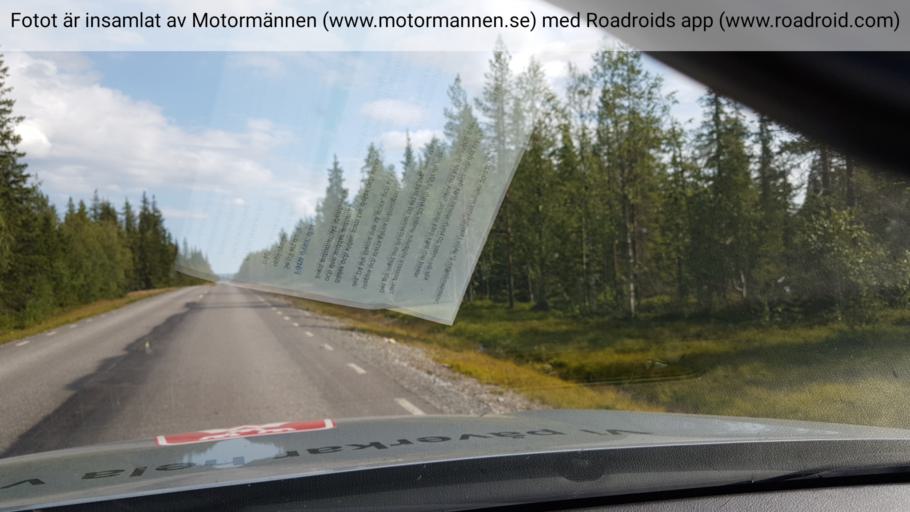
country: SE
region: Vaesterbotten
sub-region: Skelleftea Kommun
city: Storvik
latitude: 65.3564
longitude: 20.4651
